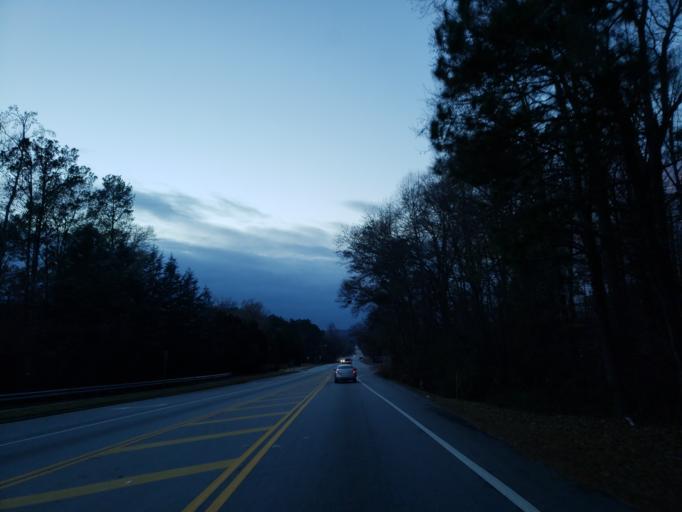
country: US
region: Georgia
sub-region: Douglas County
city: Lithia Springs
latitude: 33.6928
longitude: -84.6188
